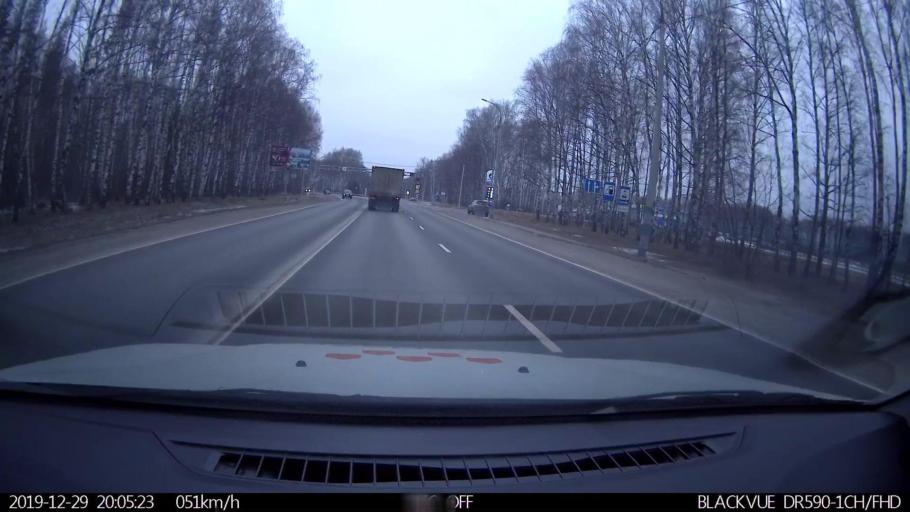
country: RU
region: Nizjnij Novgorod
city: Neklyudovo
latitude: 56.3908
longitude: 44.0107
